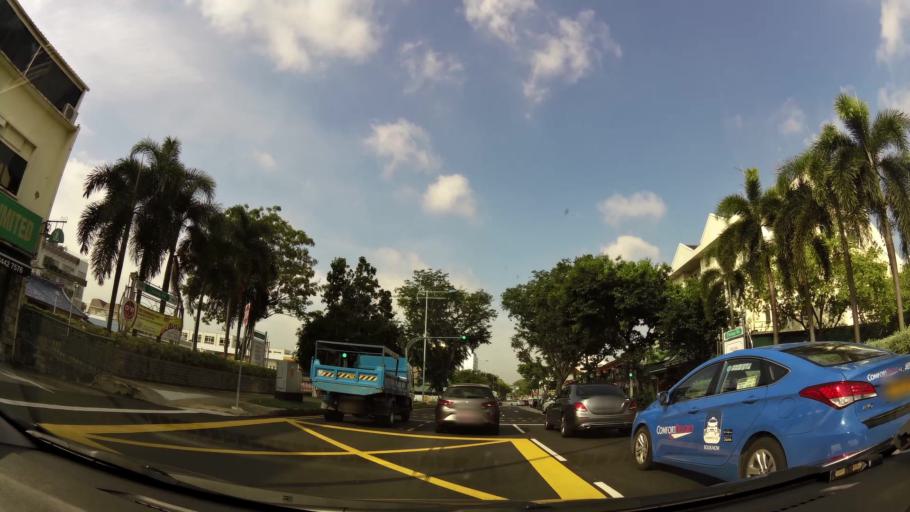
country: SG
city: Singapore
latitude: 1.3193
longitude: 103.9134
